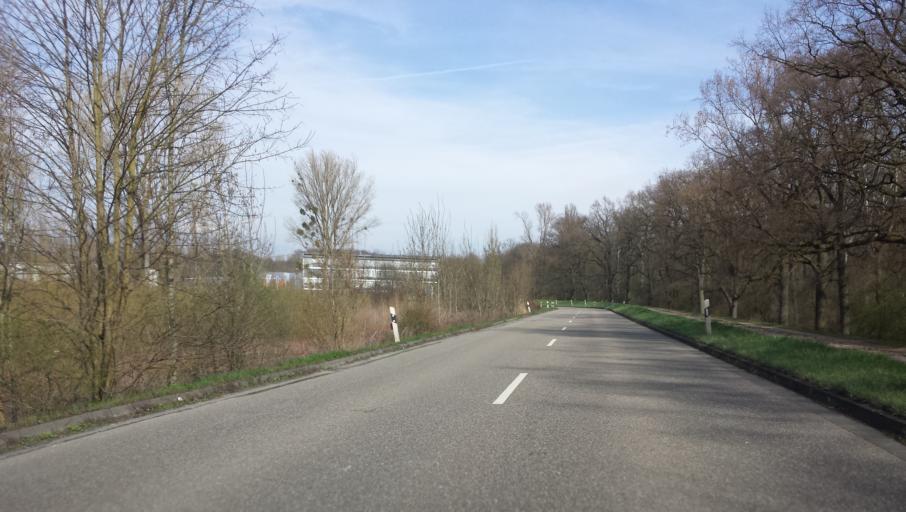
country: DE
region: Baden-Wuerttemberg
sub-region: Karlsruhe Region
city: Oberhausen-Rheinhausen
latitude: 49.2893
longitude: 8.4752
